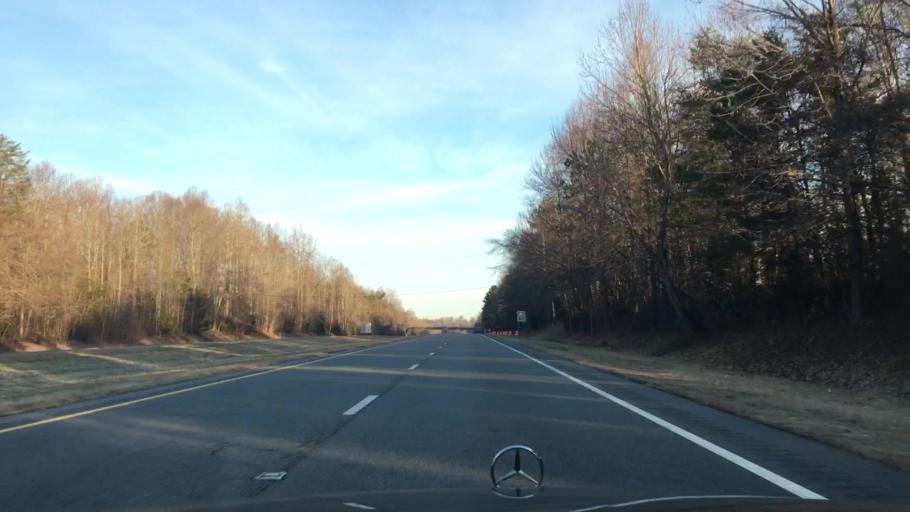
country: US
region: North Carolina
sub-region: Guilford County
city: Pleasant Garden
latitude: 36.0081
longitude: -79.7583
